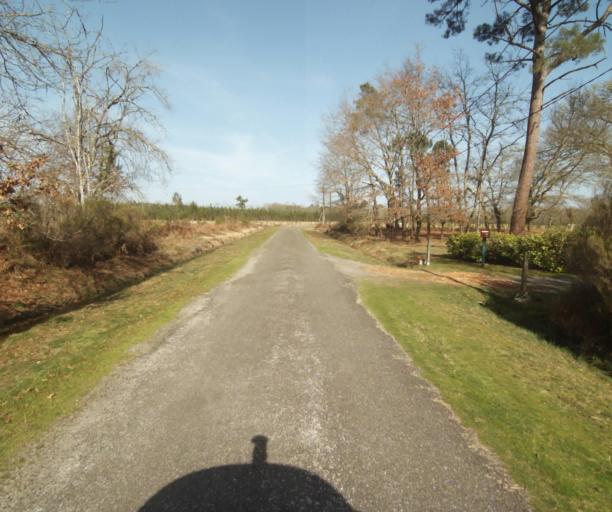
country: FR
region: Aquitaine
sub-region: Departement des Landes
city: Roquefort
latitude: 44.1333
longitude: -0.2088
